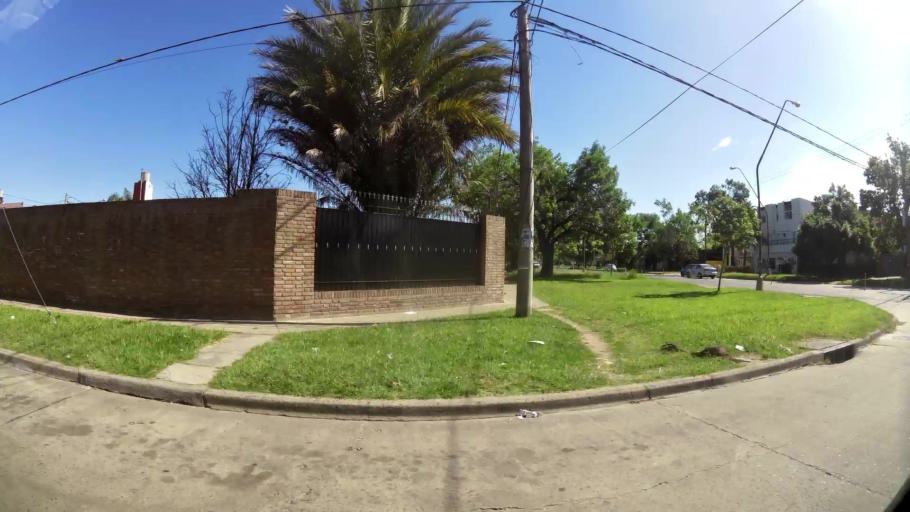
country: AR
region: Santa Fe
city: Santa Fe de la Vera Cruz
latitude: -31.6091
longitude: -60.6775
